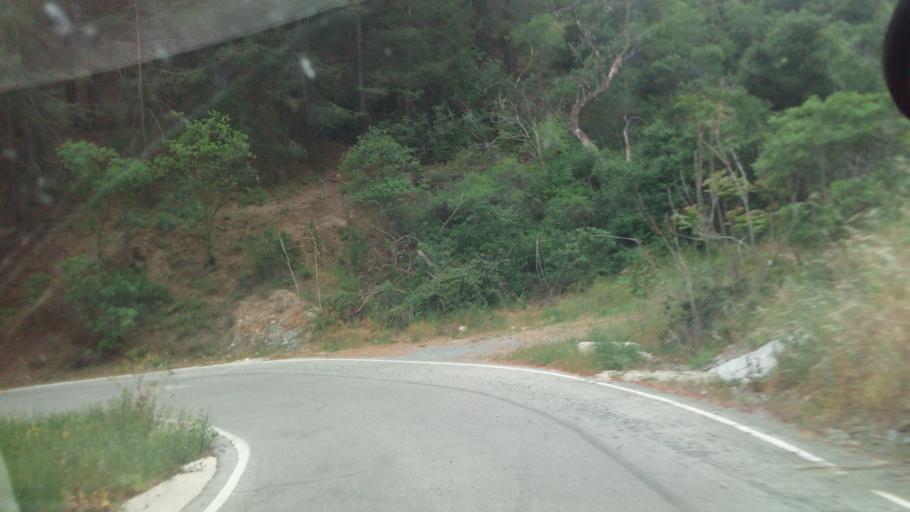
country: CY
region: Lefkosia
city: Kakopetria
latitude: 34.9640
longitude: 32.7459
